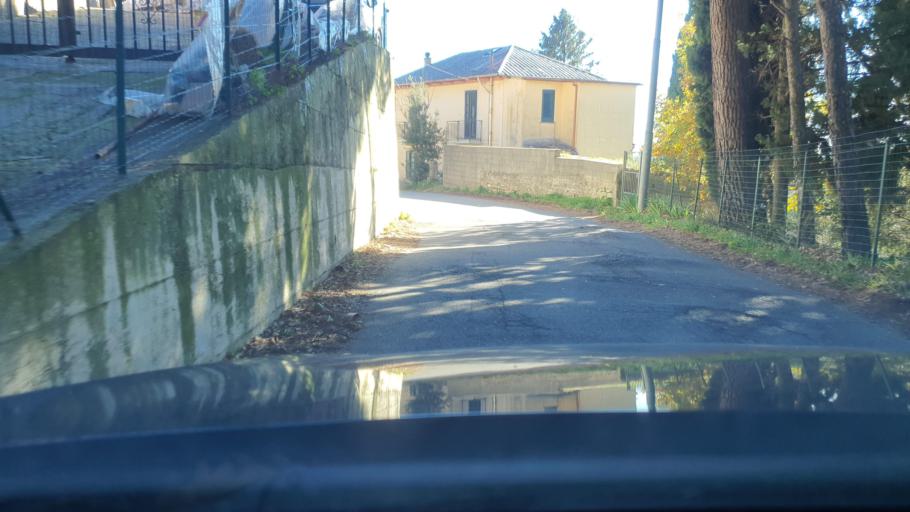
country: IT
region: Calabria
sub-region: Provincia di Catanzaro
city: Sant'Elia
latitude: 38.9587
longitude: 16.5784
